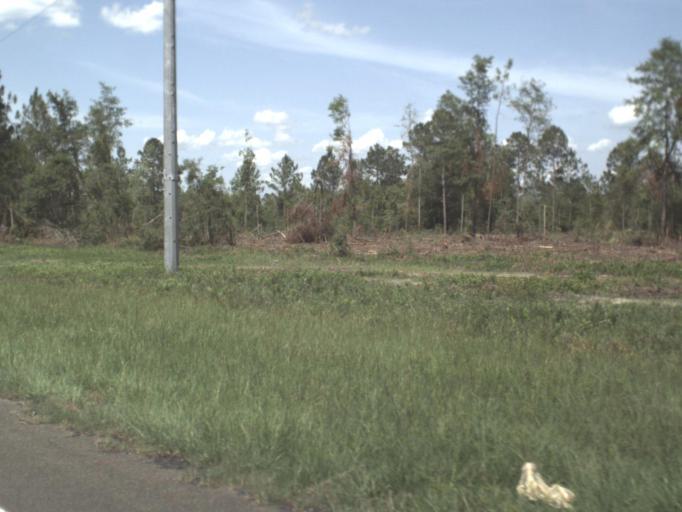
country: US
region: Florida
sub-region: Gilchrist County
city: Trenton
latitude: 29.6892
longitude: -82.7642
